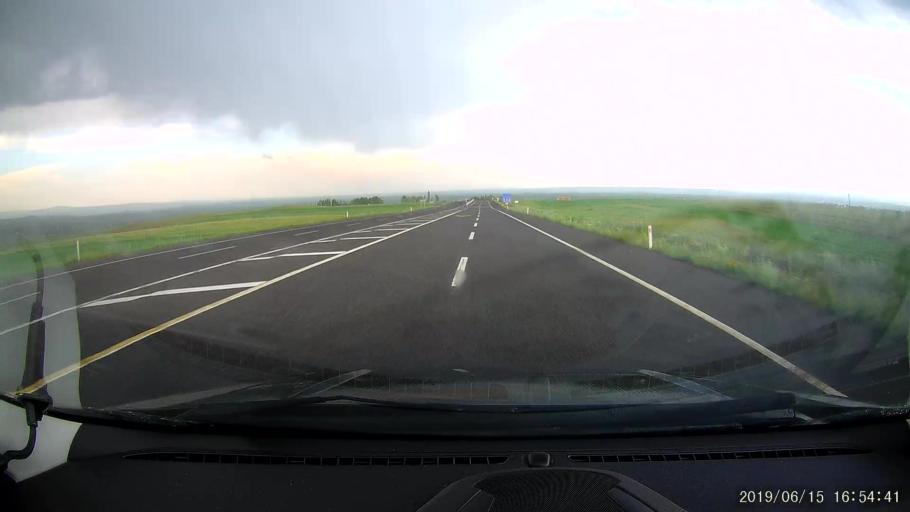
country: TR
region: Kars
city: Susuz
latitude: 40.7892
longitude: 43.1294
